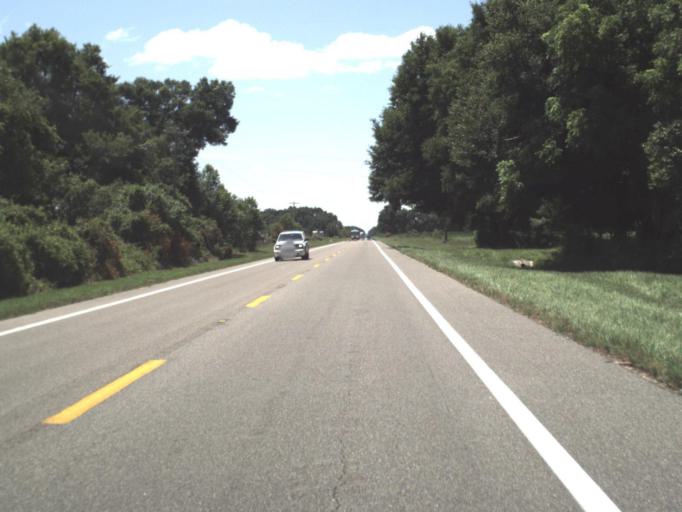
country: US
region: Florida
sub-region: Lafayette County
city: Mayo
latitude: 29.9951
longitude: -83.0134
